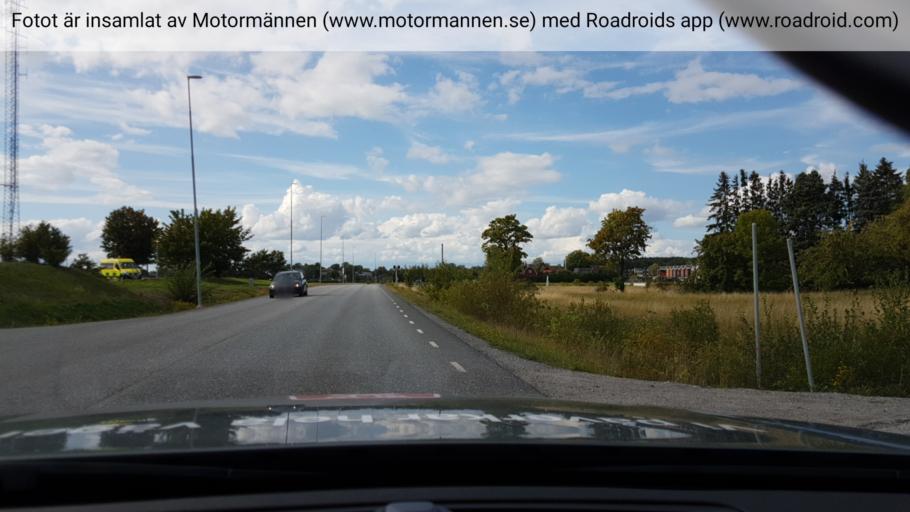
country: SE
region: Stockholm
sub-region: Upplands-Bro Kommun
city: Bro
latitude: 59.5069
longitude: 17.6600
